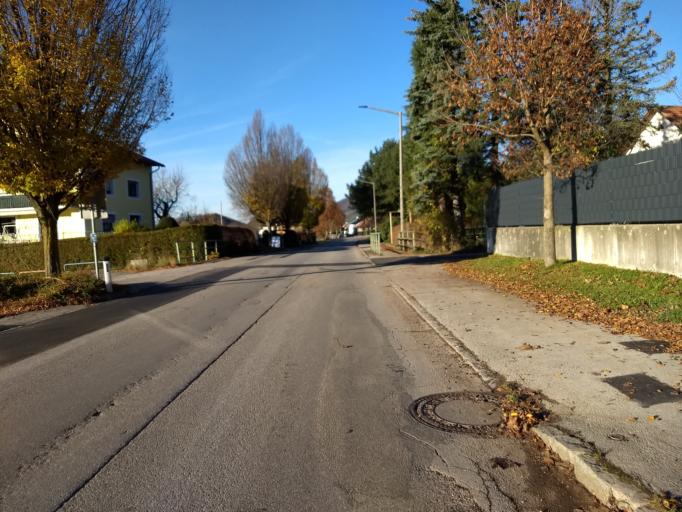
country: AT
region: Upper Austria
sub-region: Politischer Bezirk Kirchdorf an der Krems
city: Micheldorf in Oberoesterreich
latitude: 47.8838
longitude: 14.1326
